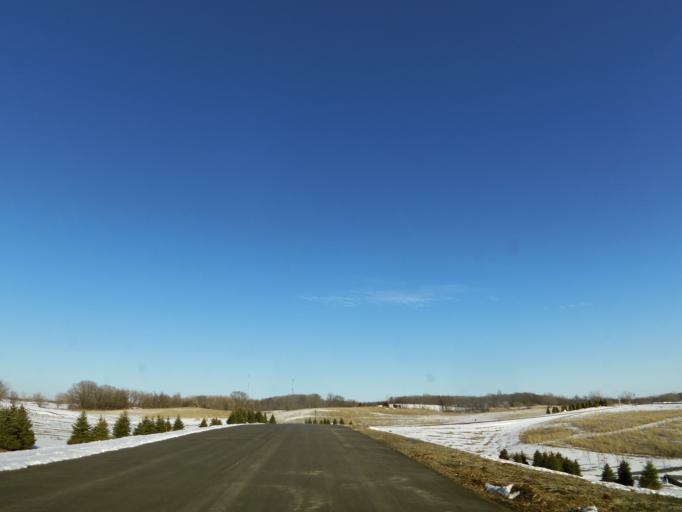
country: US
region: Minnesota
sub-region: Scott County
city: Elko New Market
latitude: 44.6292
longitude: -93.3640
